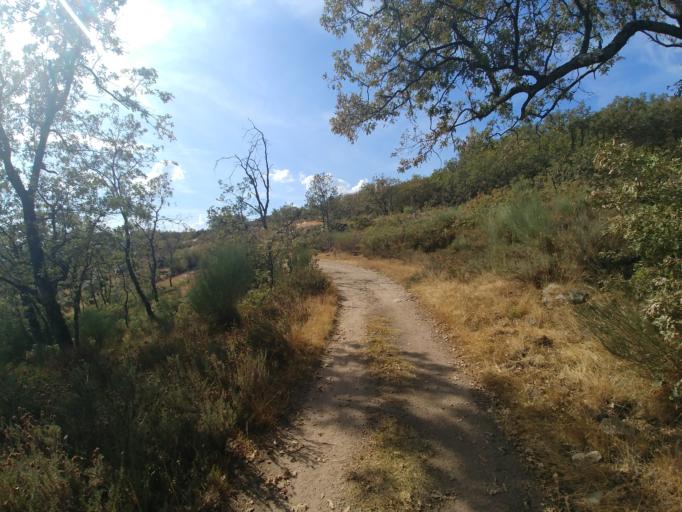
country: ES
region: Extremadura
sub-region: Provincia de Caceres
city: Garganta la Olla
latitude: 40.0942
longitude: -5.7553
